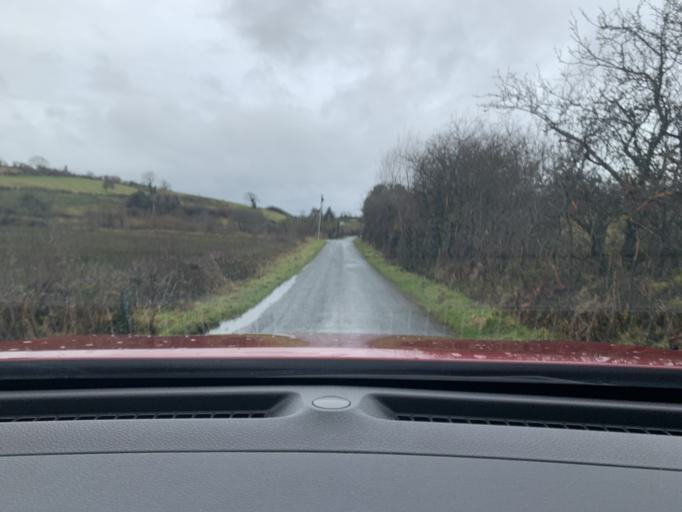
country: IE
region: Connaught
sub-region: Sligo
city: Sligo
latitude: 54.2086
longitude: -8.3934
